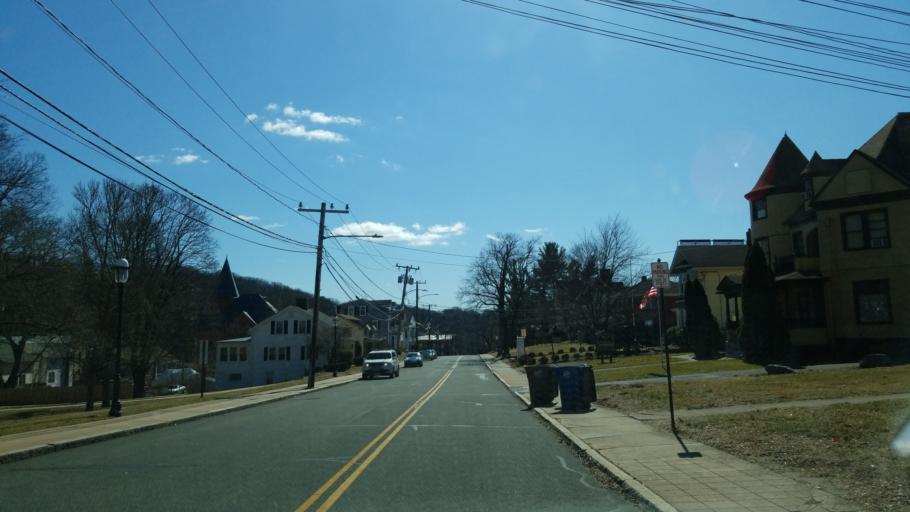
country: US
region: Connecticut
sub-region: Tolland County
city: Rockville
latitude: 41.8698
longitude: -72.4497
